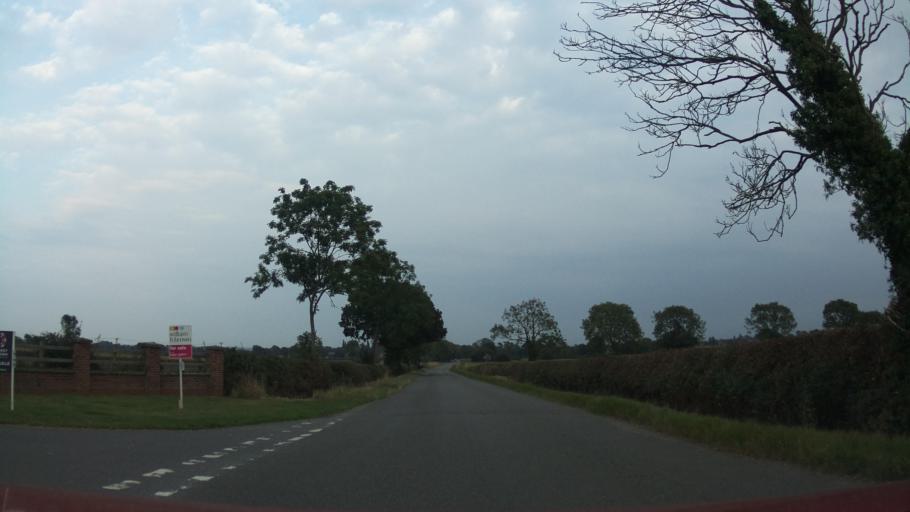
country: GB
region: England
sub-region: Lincolnshire
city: Skellingthorpe
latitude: 53.1431
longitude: -0.6617
